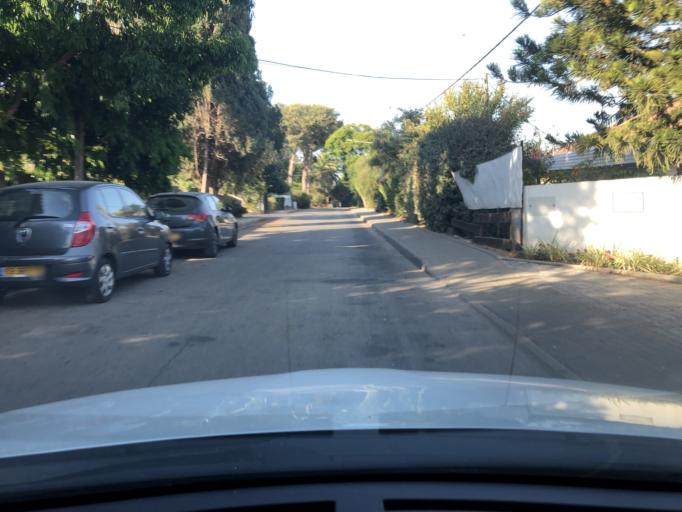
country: IL
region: Central District
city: Hod HaSharon
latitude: 32.1417
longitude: 34.9034
